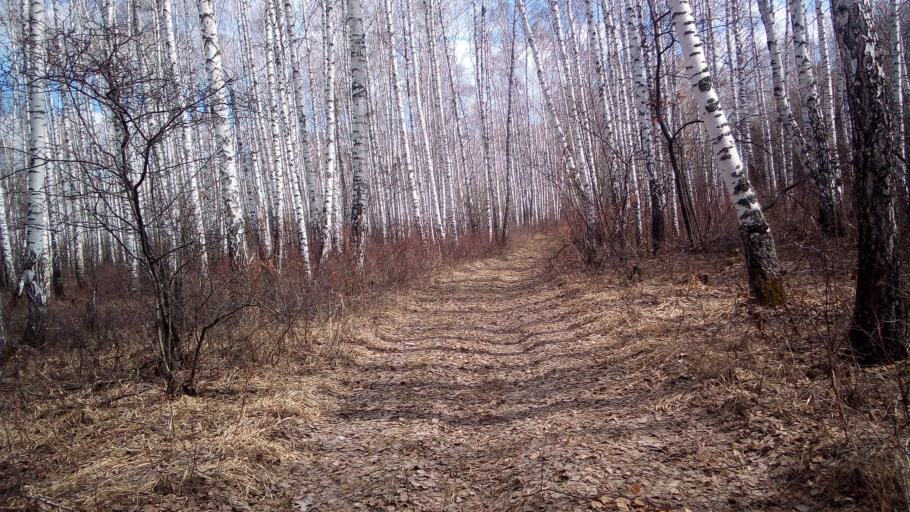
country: RU
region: Chelyabinsk
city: Sargazy
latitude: 55.1236
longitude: 61.2530
